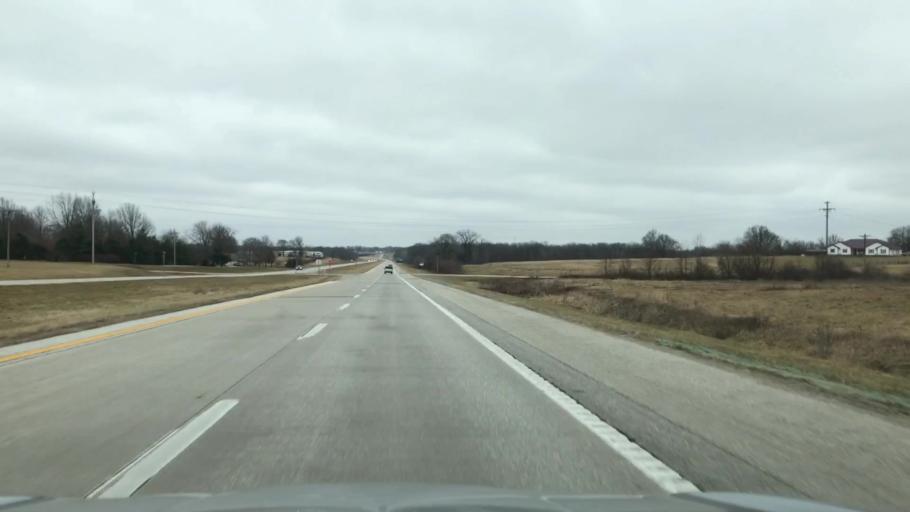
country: US
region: Missouri
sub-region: Linn County
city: Brookfield
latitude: 39.7790
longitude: -93.1010
